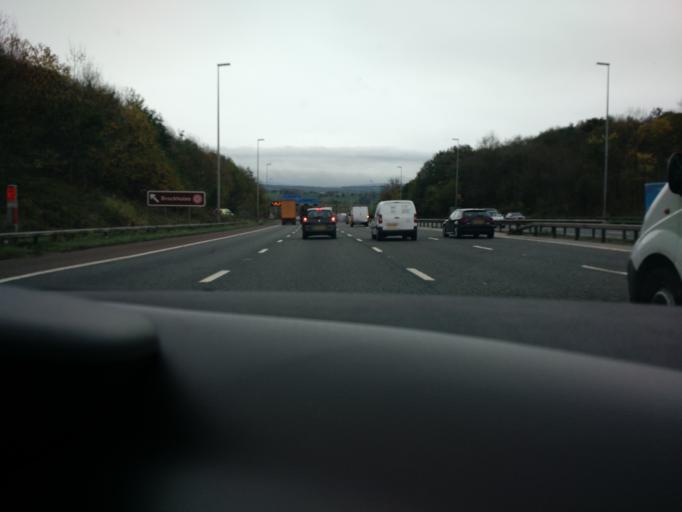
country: GB
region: England
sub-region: Lancashire
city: Goosnargh
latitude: 53.7763
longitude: -2.6443
